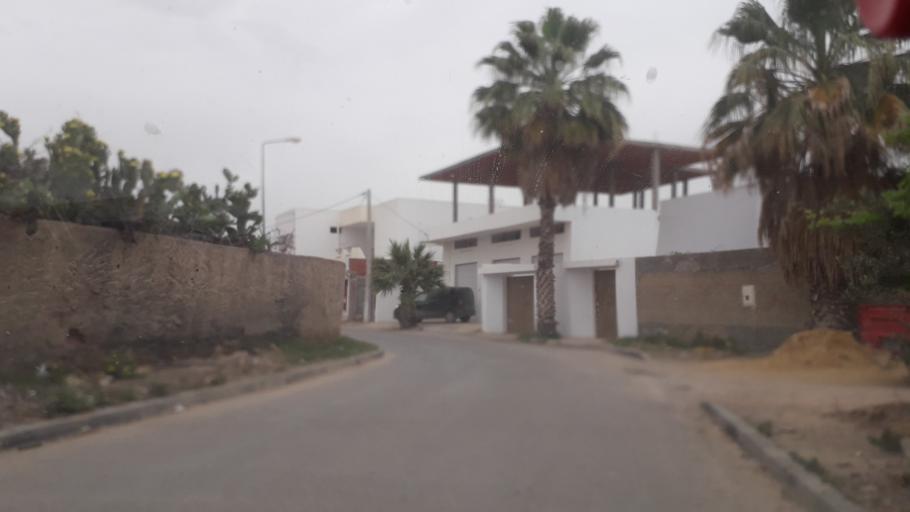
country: TN
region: Safaqis
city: Al Qarmadah
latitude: 34.7932
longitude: 10.7693
